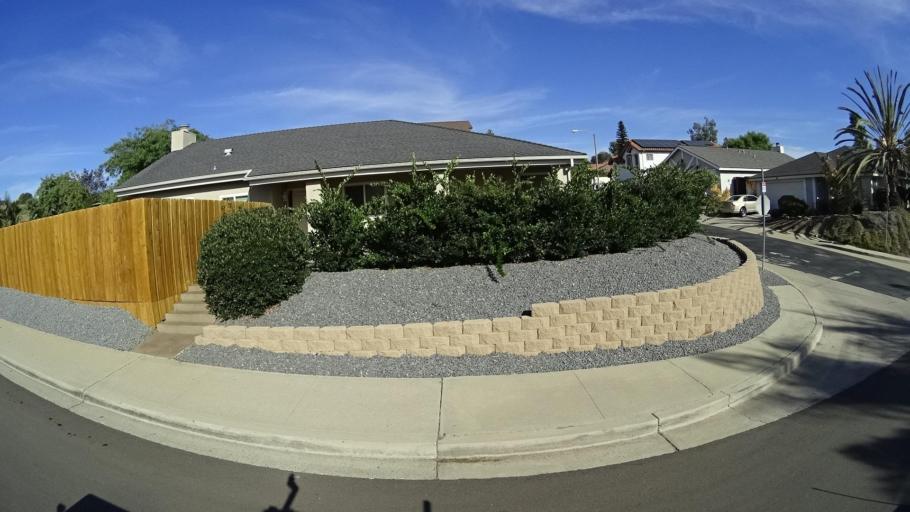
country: US
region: California
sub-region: San Diego County
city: Casa de Oro-Mount Helix
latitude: 32.7338
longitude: -116.9654
